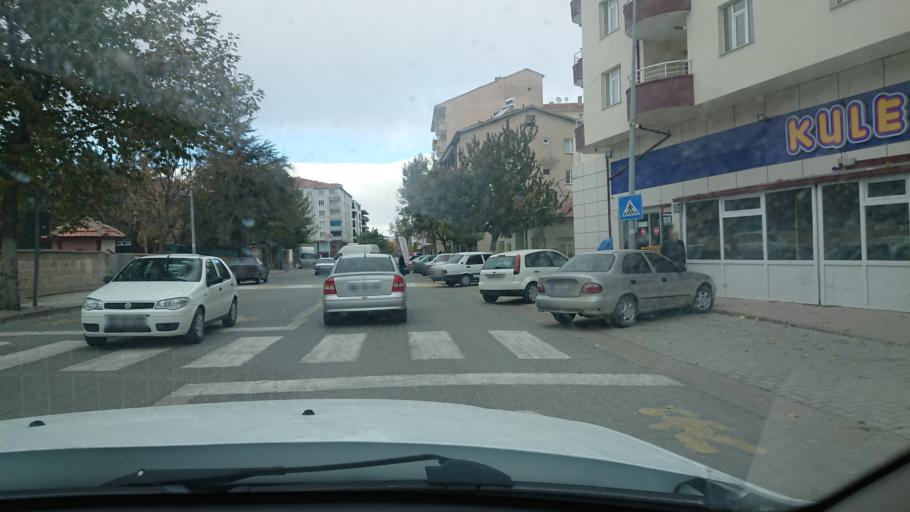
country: TR
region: Aksaray
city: Ortakoy
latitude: 38.7377
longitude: 34.0387
